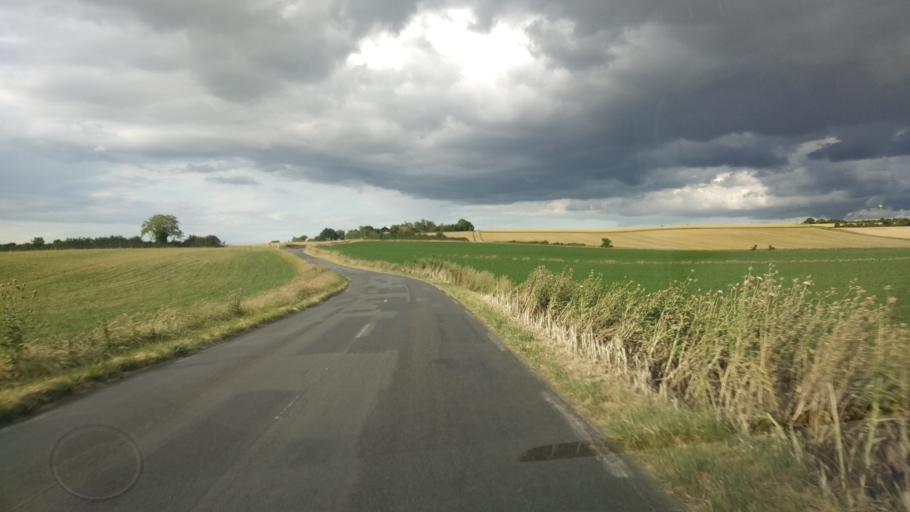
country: FR
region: Poitou-Charentes
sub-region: Departement de la Vienne
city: Migne-Auxances
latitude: 46.6233
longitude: 0.3260
